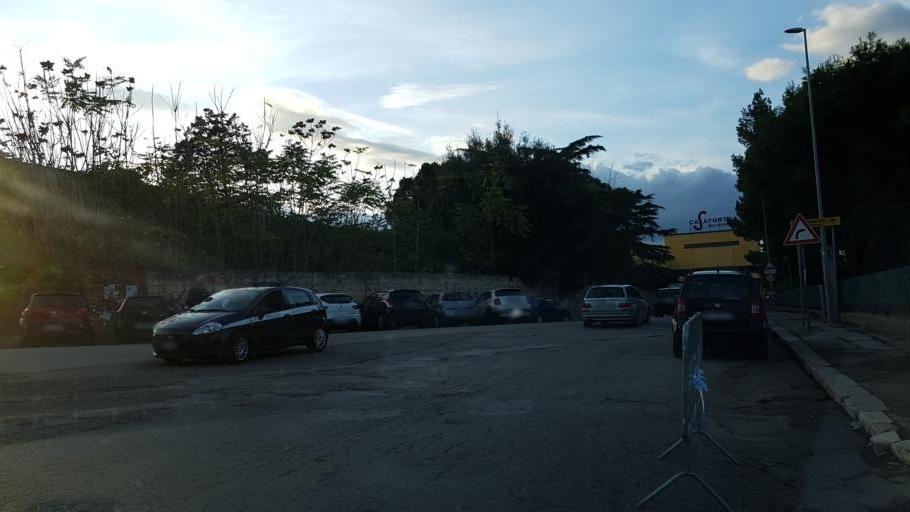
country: IT
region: Apulia
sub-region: Provincia di Foggia
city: Foggia
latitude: 41.4701
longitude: 15.5492
